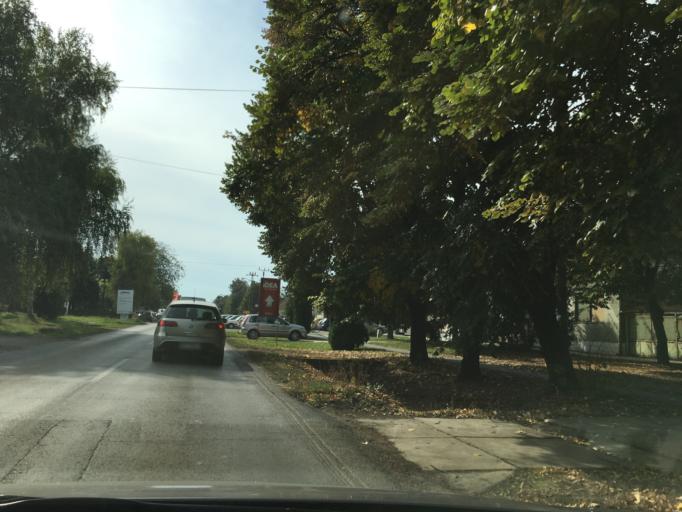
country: RS
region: Autonomna Pokrajina Vojvodina
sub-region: Juznobacki Okrug
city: Temerin
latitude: 45.4187
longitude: 19.8926
